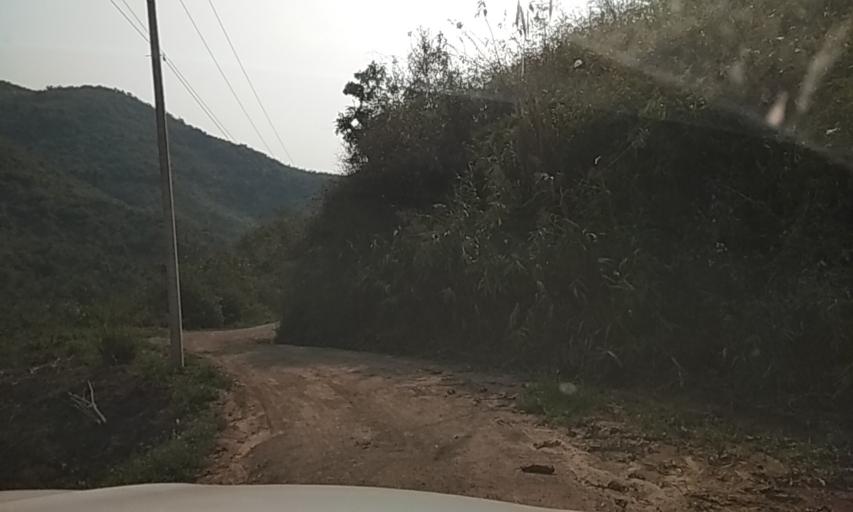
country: LA
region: Louangphabang
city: Louangphabang
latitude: 20.0469
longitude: 101.8454
